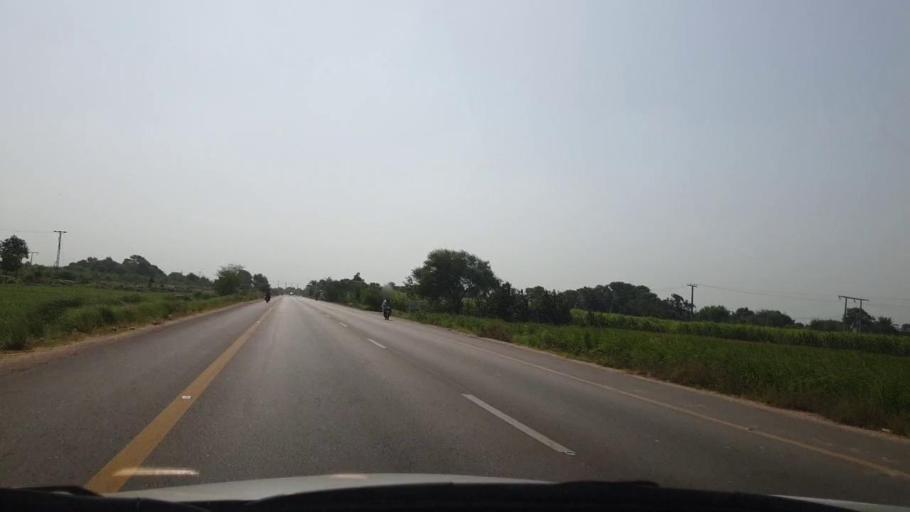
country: PK
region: Sindh
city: Matli
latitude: 25.0863
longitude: 68.6043
